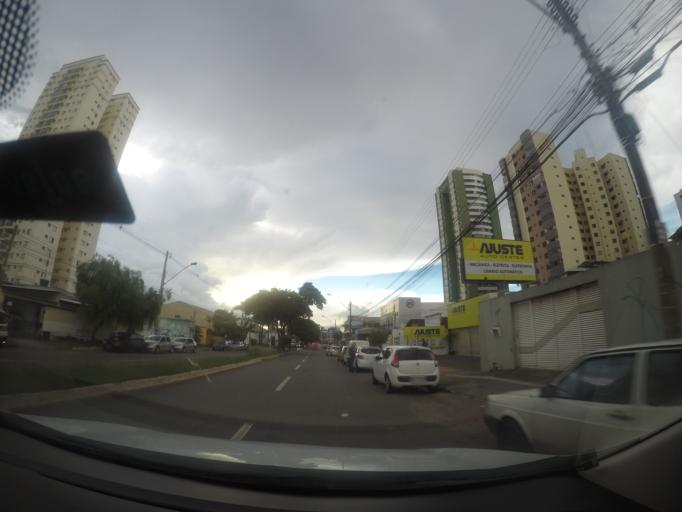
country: BR
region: Goias
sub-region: Goiania
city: Goiania
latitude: -16.6899
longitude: -49.2799
